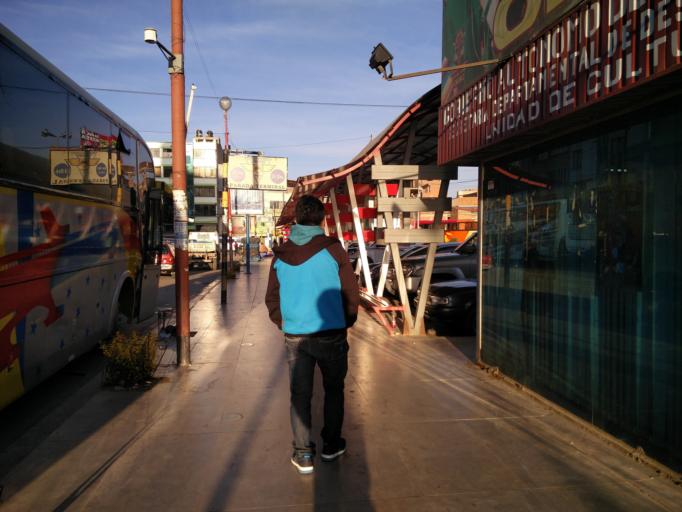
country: BO
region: Oruro
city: Oruro
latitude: -17.9622
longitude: -67.1042
